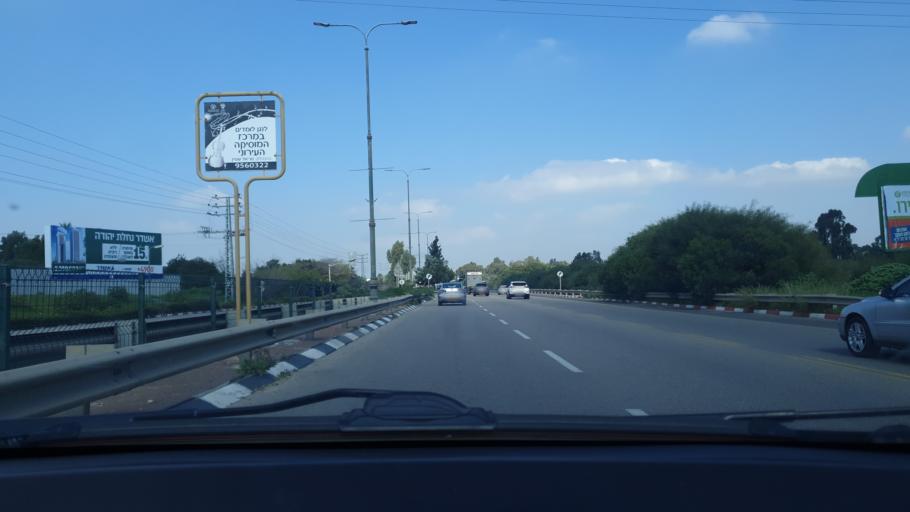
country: IL
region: Central District
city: Bet Dagan
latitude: 31.9849
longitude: 34.8107
